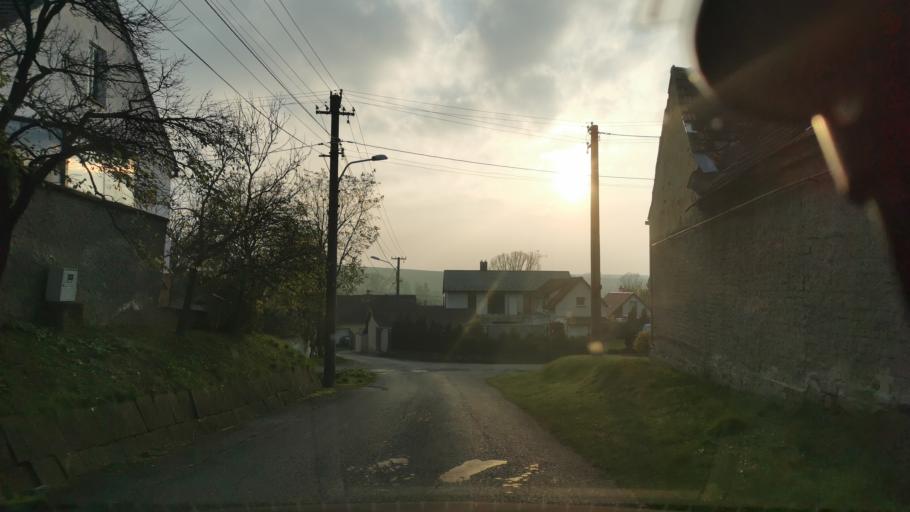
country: SK
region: Trnavsky
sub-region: Okres Skalica
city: Skalica
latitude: 48.7894
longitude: 17.2181
